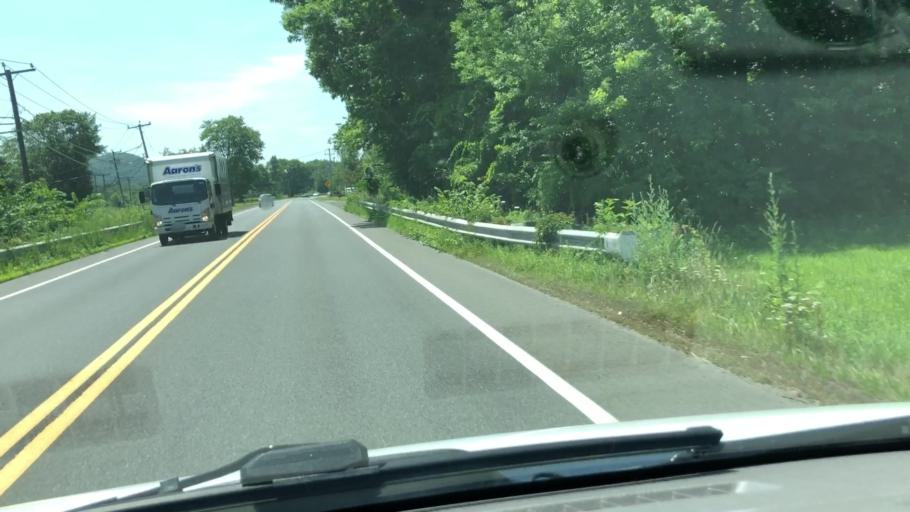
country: US
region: Massachusetts
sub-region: Franklin County
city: South Deerfield
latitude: 42.5113
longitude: -72.6055
